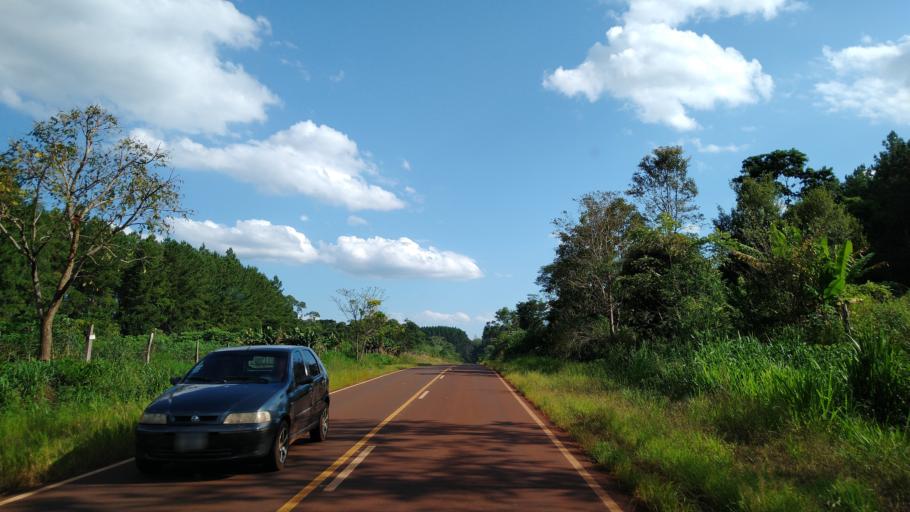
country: AR
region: Misiones
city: Puerto Piray
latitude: -26.4869
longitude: -54.6746
